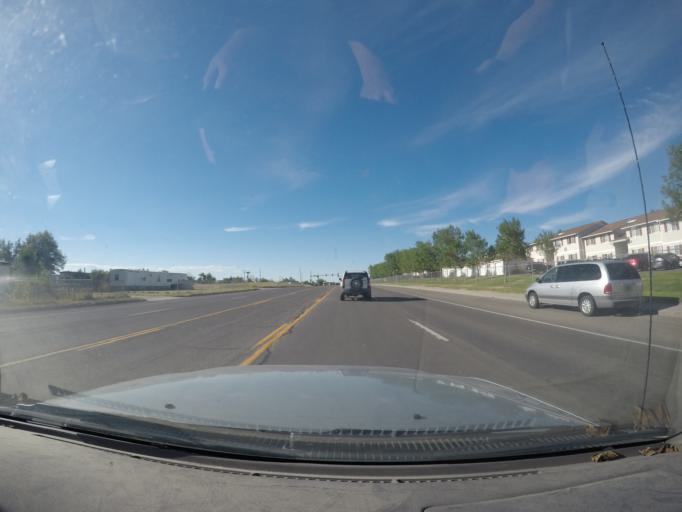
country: US
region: Wyoming
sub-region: Laramie County
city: Fox Farm-College
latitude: 41.1438
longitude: -104.7611
